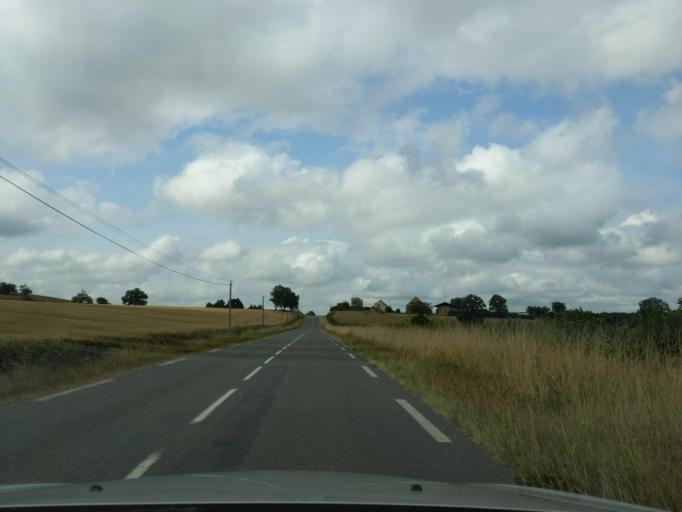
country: FR
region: Bourgogne
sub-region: Departement de la Nievre
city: Luzy
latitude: 46.7392
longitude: 3.9295
